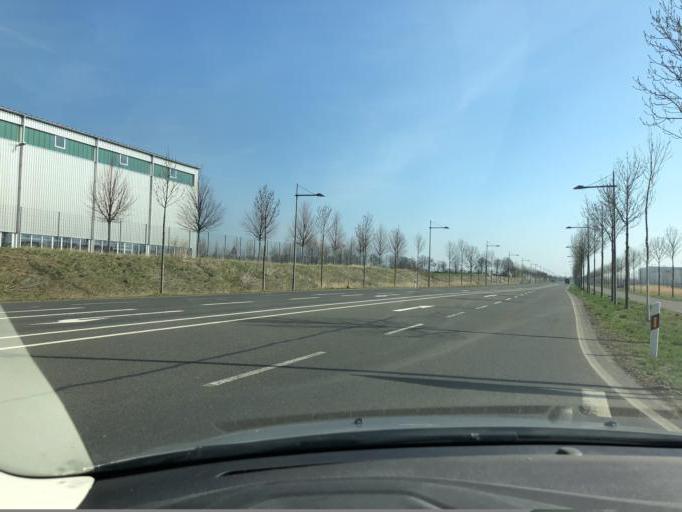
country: DE
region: Saxony
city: Taucha
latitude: 51.4119
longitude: 12.4406
